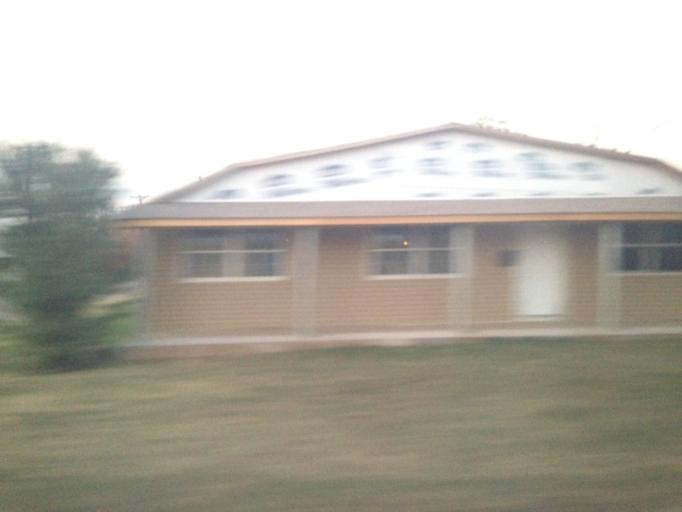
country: US
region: Texas
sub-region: Taylor County
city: Abilene
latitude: 32.4475
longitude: -99.7535
